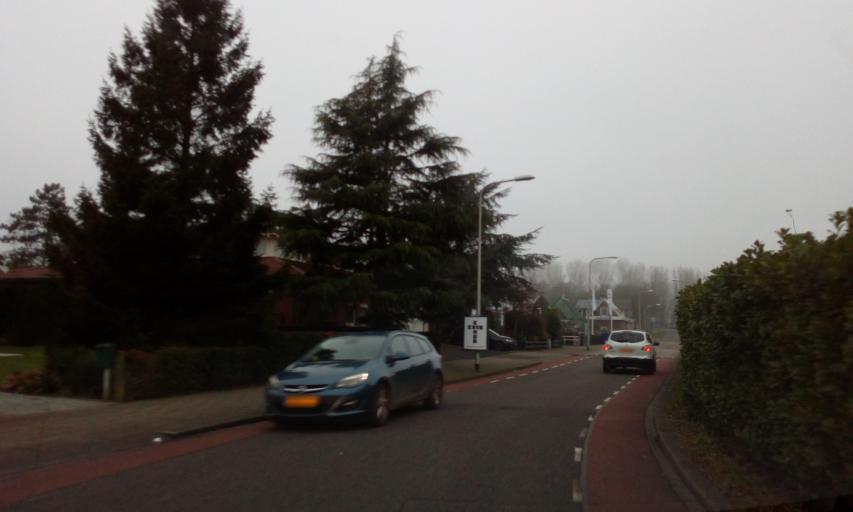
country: NL
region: South Holland
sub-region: Gemeente Capelle aan den IJssel
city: Capelle aan den IJssel
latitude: 51.9711
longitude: 4.6087
